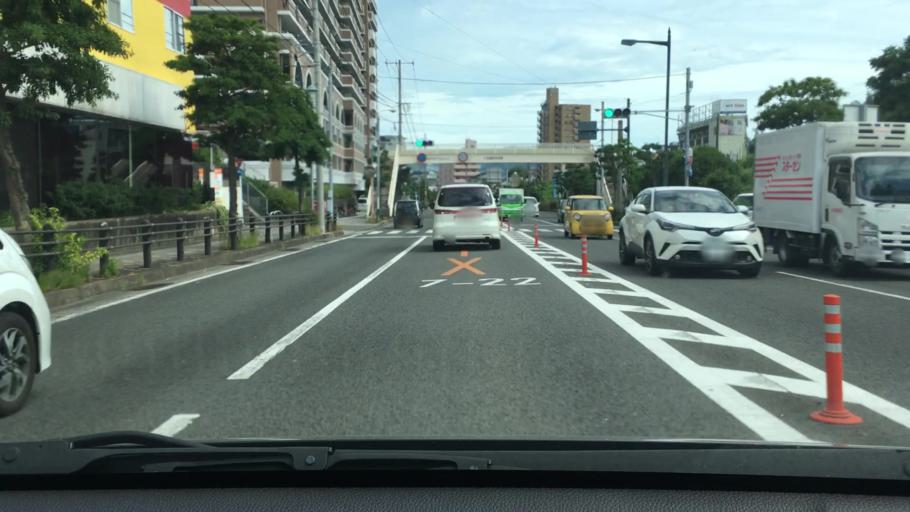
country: JP
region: Nagasaki
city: Obita
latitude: 32.7983
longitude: 129.8542
